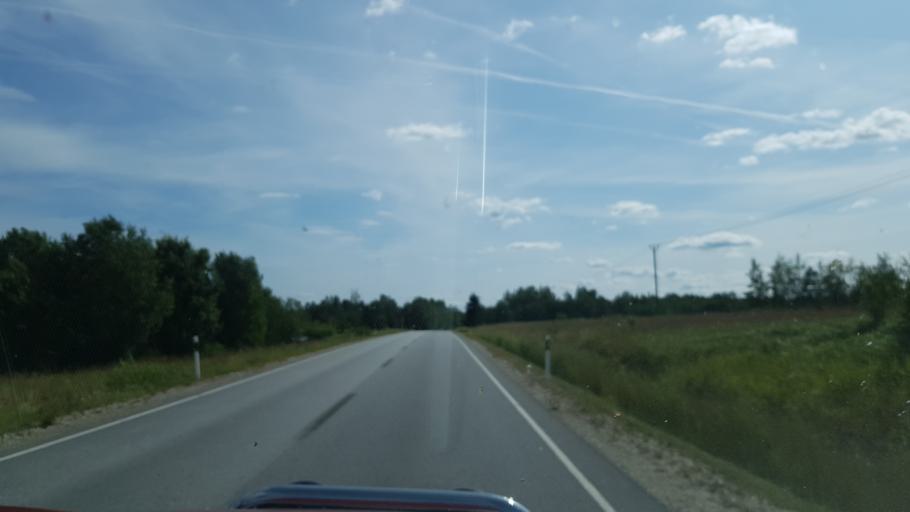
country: EE
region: Jogevamaa
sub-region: Mustvee linn
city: Mustvee
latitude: 58.9321
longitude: 26.8183
